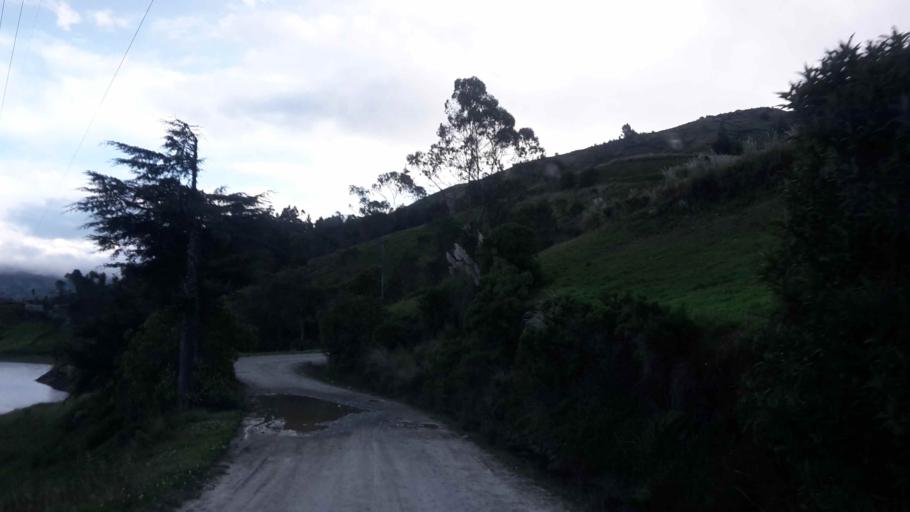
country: BO
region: Cochabamba
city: Colomi
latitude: -17.2644
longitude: -65.9056
